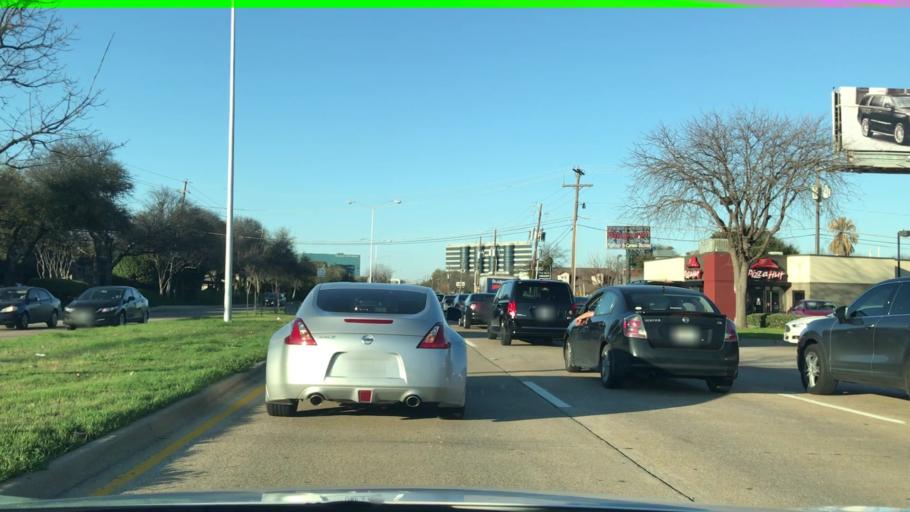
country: US
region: Texas
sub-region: Dallas County
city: Addison
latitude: 32.9910
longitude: -96.8013
